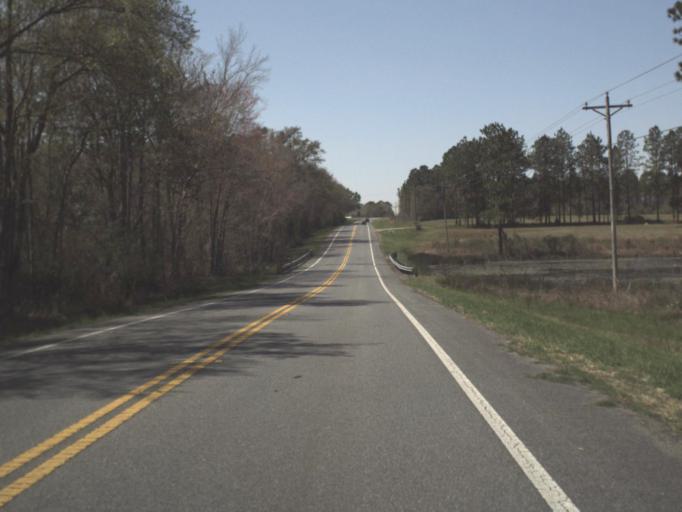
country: US
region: Alabama
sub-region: Geneva County
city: Geneva
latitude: 30.9550
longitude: -85.9108
